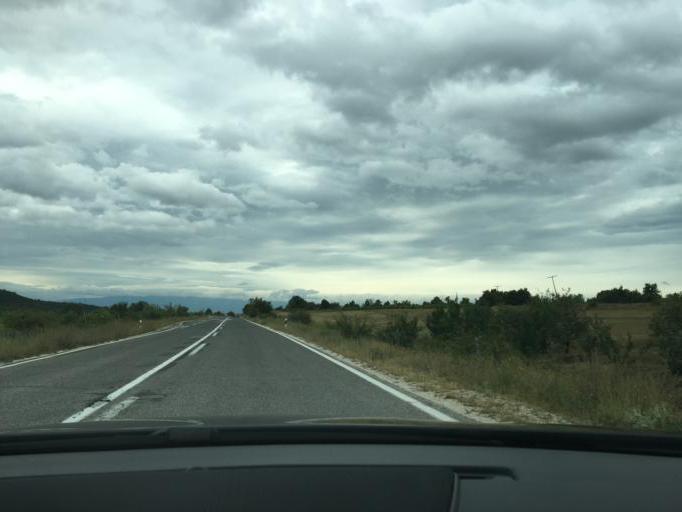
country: MK
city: Klechovce
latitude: 42.1493
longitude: 21.9713
